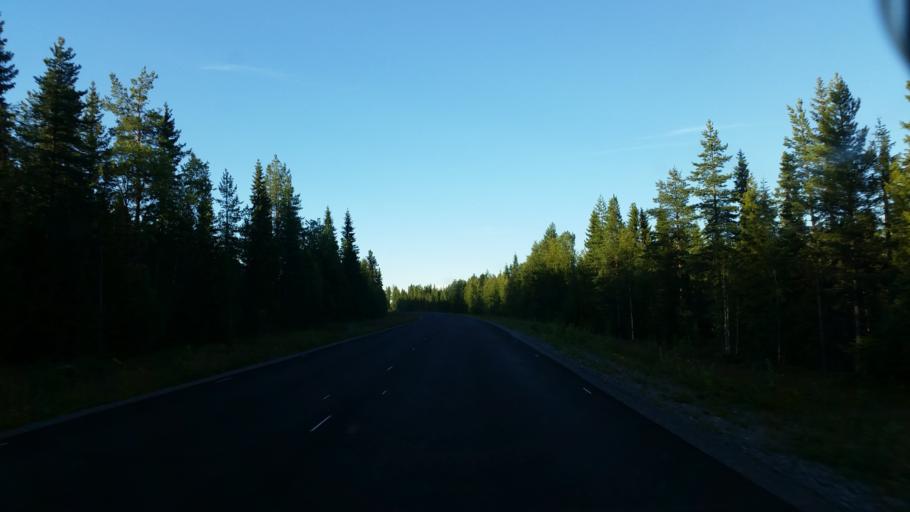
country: SE
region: Vaesterbotten
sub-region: Dorotea Kommun
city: Dorotea
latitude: 64.3088
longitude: 16.6004
